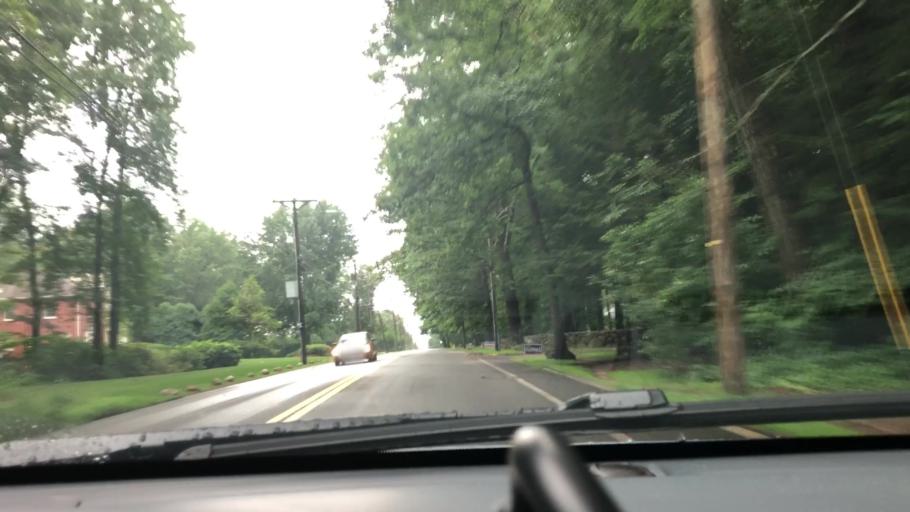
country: US
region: New Hampshire
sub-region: Hillsborough County
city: Manchester
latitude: 43.0218
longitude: -71.4622
